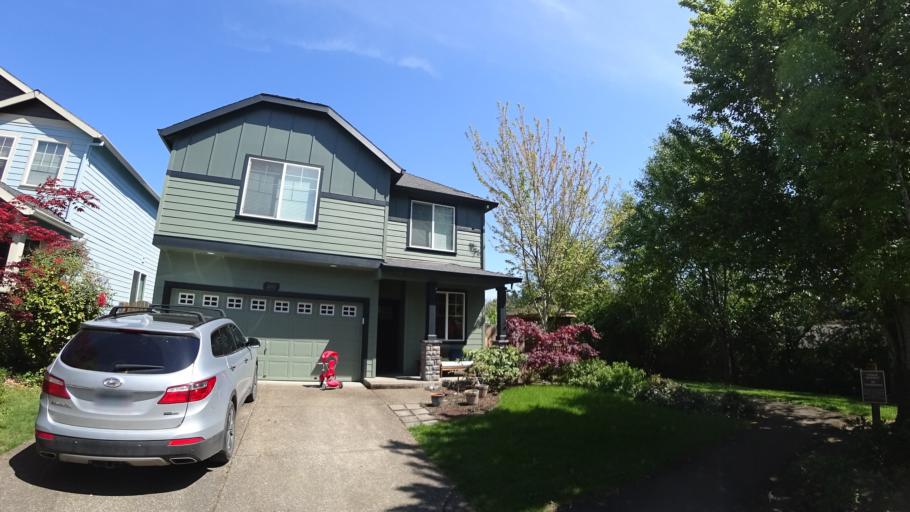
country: US
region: Oregon
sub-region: Washington County
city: Hillsboro
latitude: 45.5193
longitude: -122.9516
